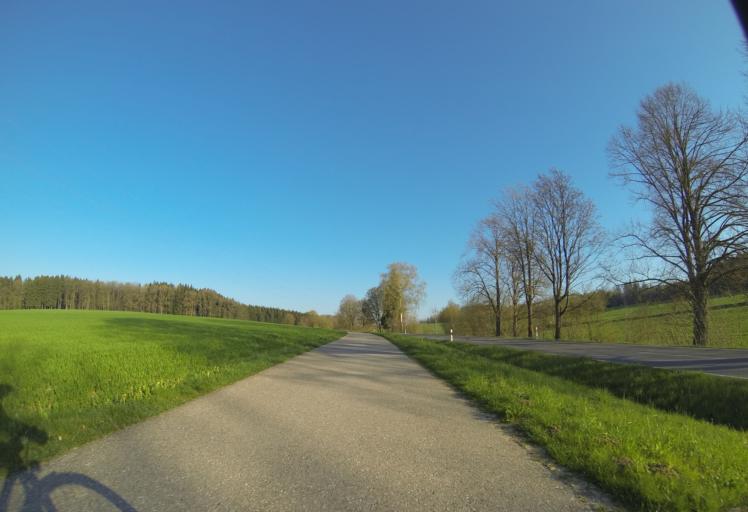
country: DE
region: Baden-Wuerttemberg
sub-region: Tuebingen Region
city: Oberdischingen
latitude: 48.3335
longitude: 9.8432
